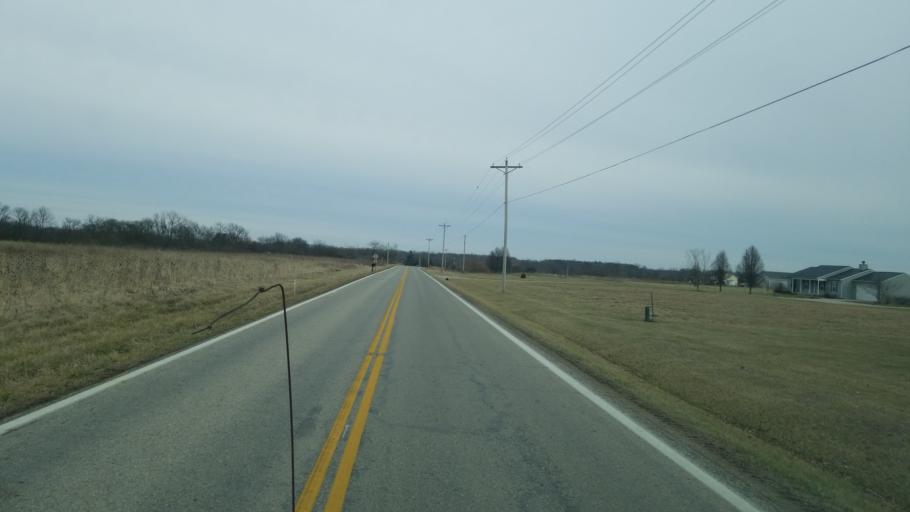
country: US
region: Ohio
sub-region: Pickaway County
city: Williamsport
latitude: 39.5490
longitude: -83.1207
